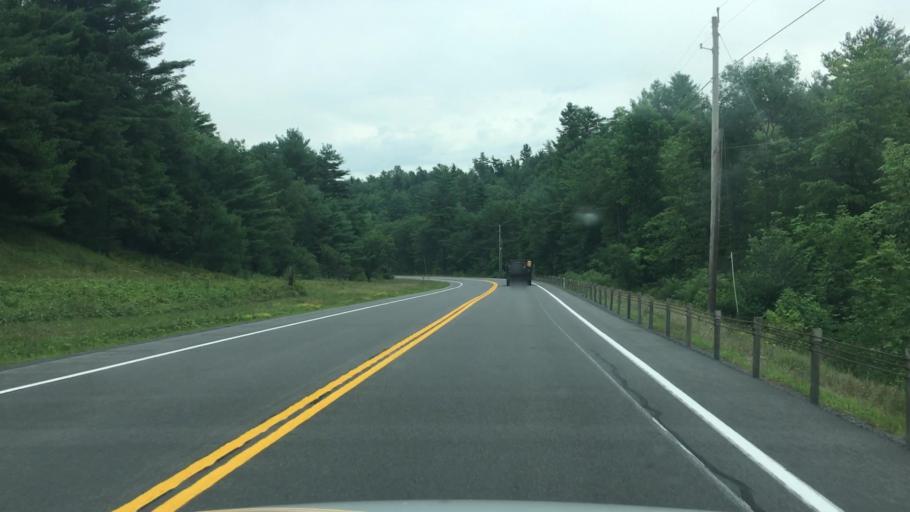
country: US
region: New York
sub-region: Essex County
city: Keeseville
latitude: 44.4555
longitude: -73.6167
